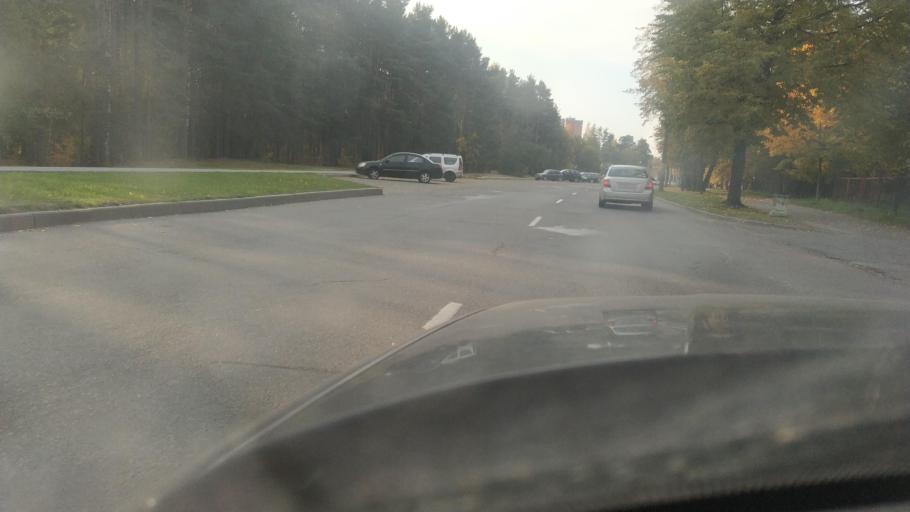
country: RU
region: Leningrad
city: Sosnovyy Bor
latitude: 59.8984
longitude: 29.1006
